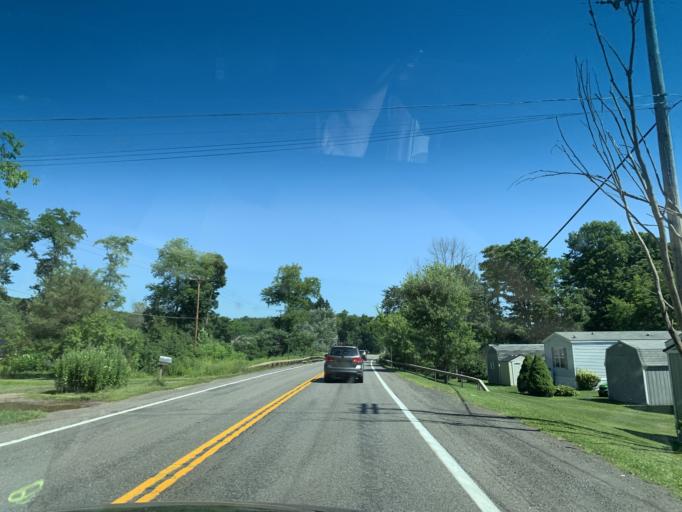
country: US
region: New York
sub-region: Delaware County
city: Sidney
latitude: 42.3323
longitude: -75.4087
